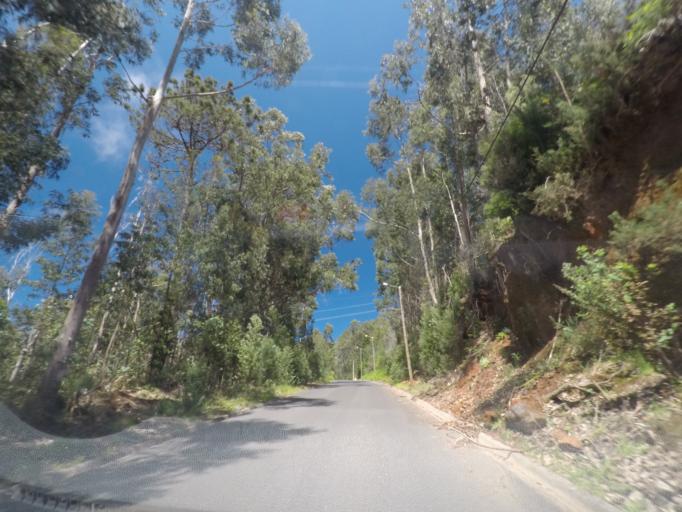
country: PT
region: Madeira
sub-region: Calheta
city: Arco da Calheta
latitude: 32.7321
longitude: -17.1315
